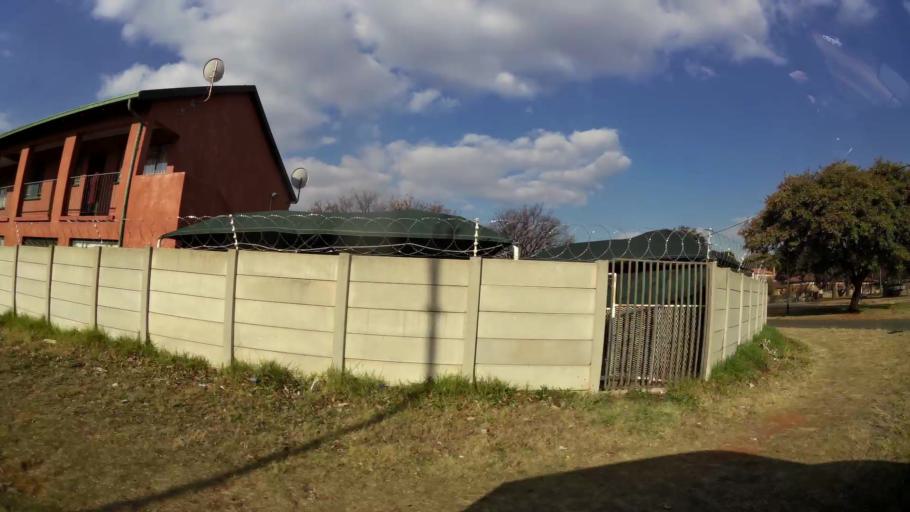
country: ZA
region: Gauteng
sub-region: West Rand District Municipality
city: Krugersdorp
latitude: -26.1001
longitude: 27.7613
